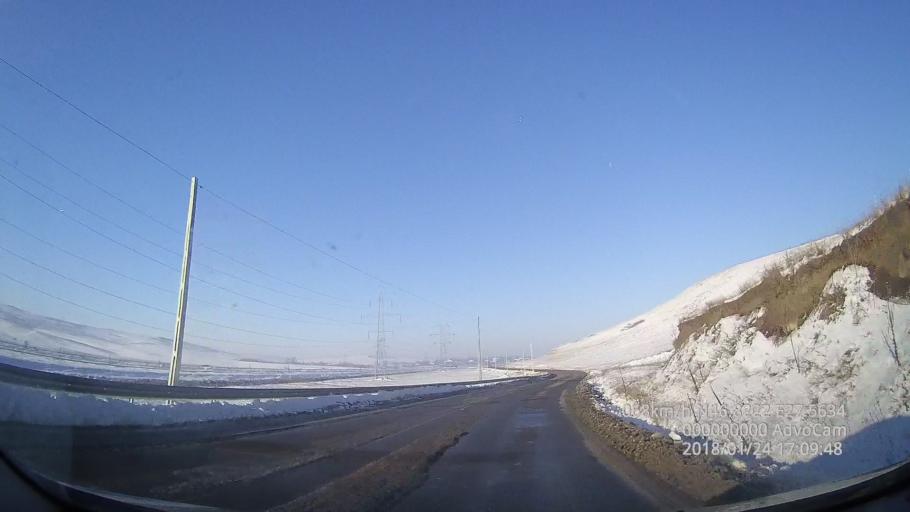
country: RO
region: Vaslui
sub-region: Comuna Vulturesti
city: Vulturesti
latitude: 46.8226
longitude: 27.5634
